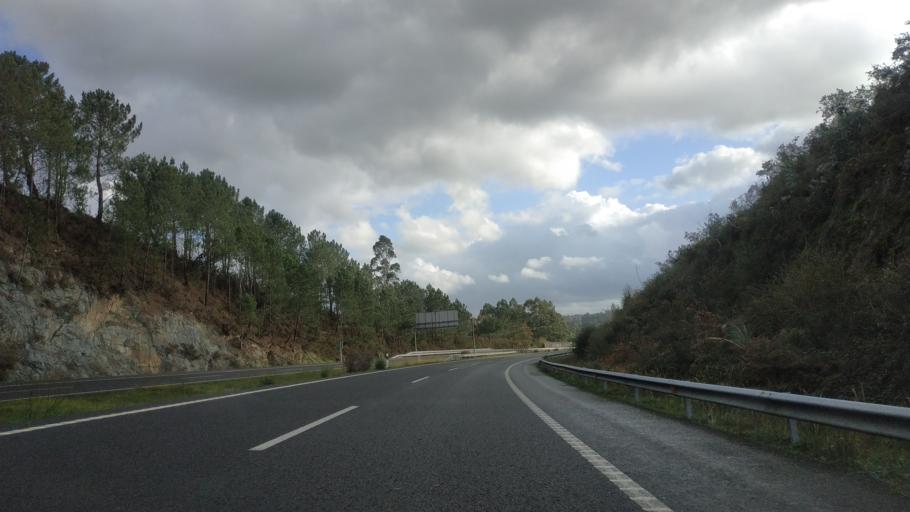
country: ES
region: Galicia
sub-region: Provincia da Coruna
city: Cambre
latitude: 43.2737
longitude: -8.3626
